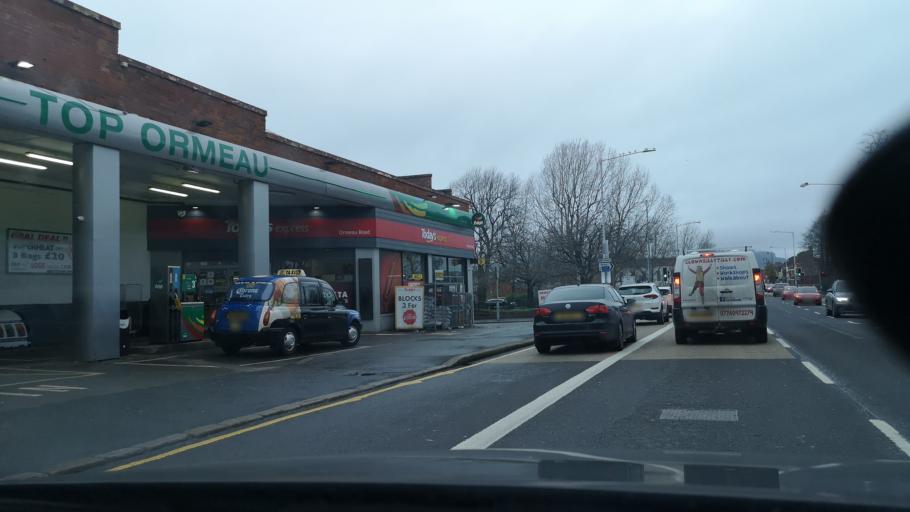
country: GB
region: Northern Ireland
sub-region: City of Belfast
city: Belfast
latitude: 54.5816
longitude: -5.9214
